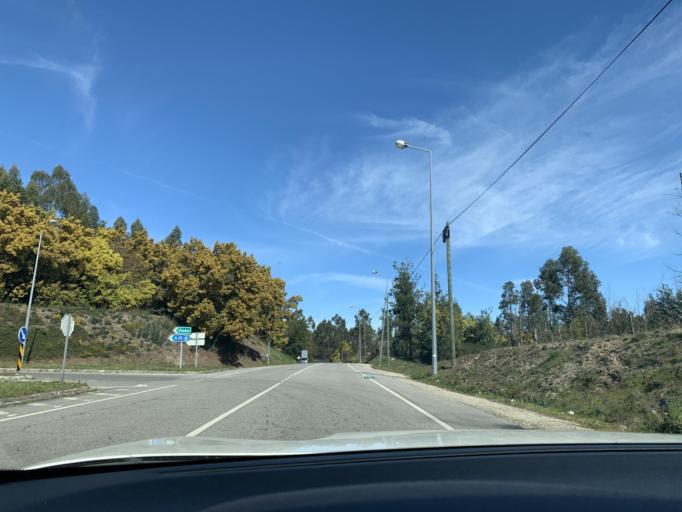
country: PT
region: Viseu
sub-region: Concelho de Tondela
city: Tondela
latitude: 40.5860
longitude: -8.0148
